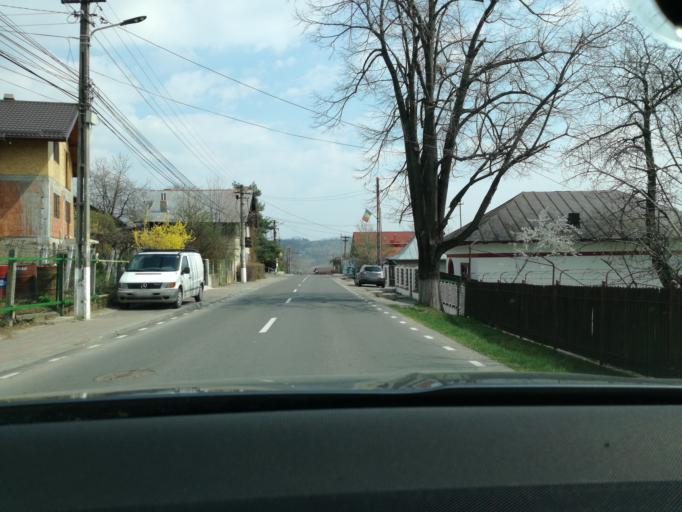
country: RO
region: Prahova
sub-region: Comuna Cornu
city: Cornu de Jos
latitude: 45.1466
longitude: 25.7095
